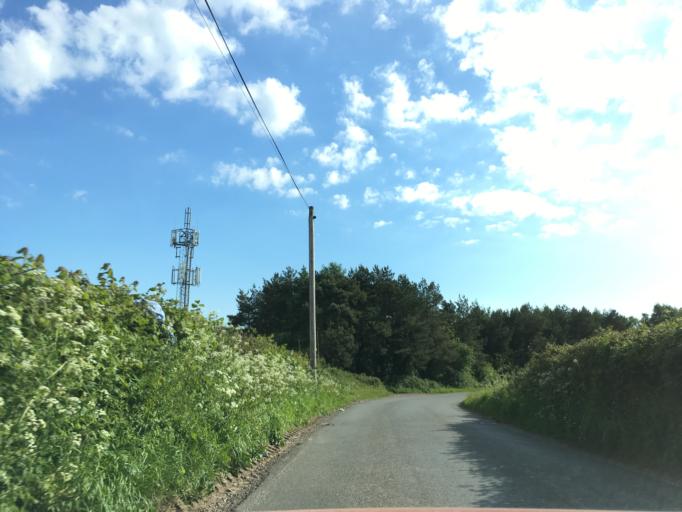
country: GB
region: Wales
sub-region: Newport
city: Marshfield
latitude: 51.5505
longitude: -3.0913
